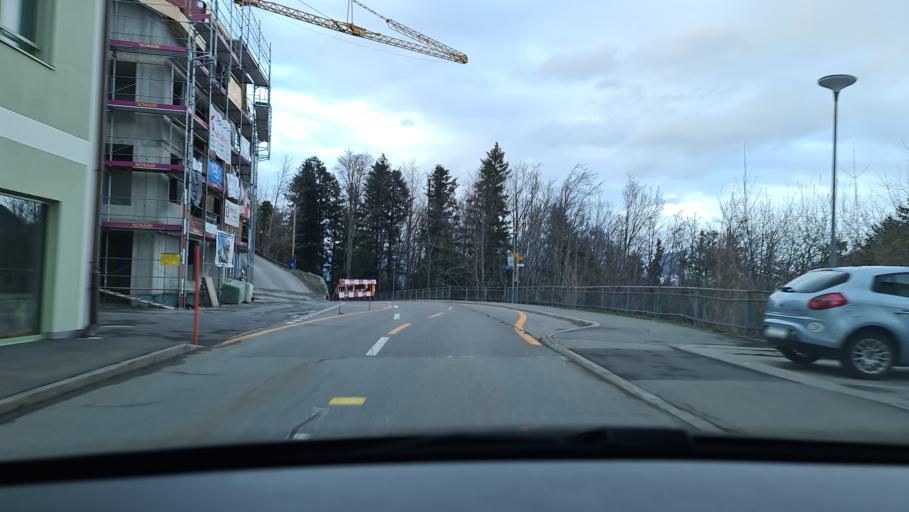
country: CH
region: Uri
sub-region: Uri
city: Bauen
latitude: 46.9681
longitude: 8.5855
